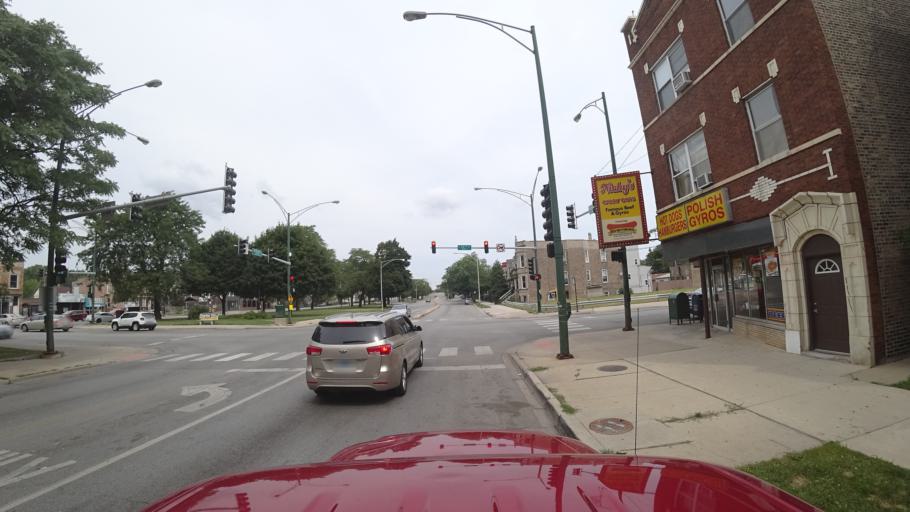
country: US
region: Illinois
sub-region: Cook County
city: Chicago
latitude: 41.8301
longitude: -87.6844
